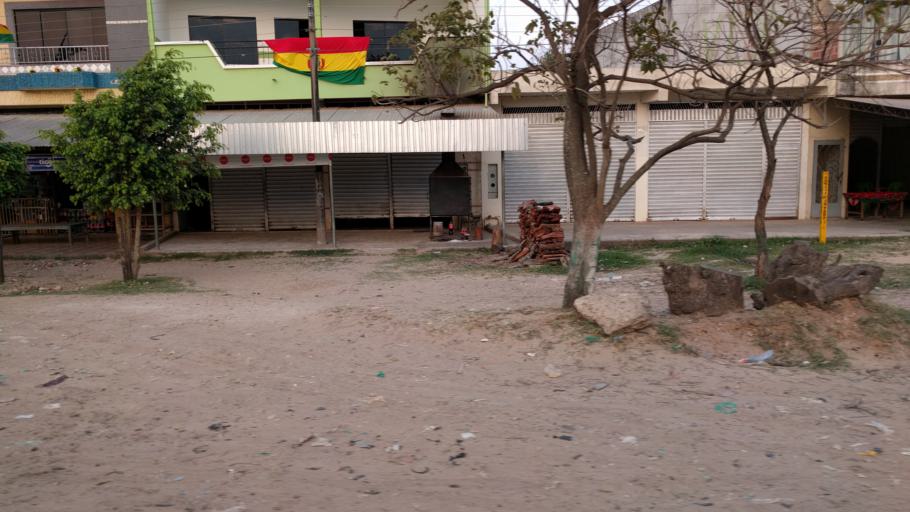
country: BO
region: Santa Cruz
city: Santa Rita
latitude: -17.9429
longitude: -63.3514
